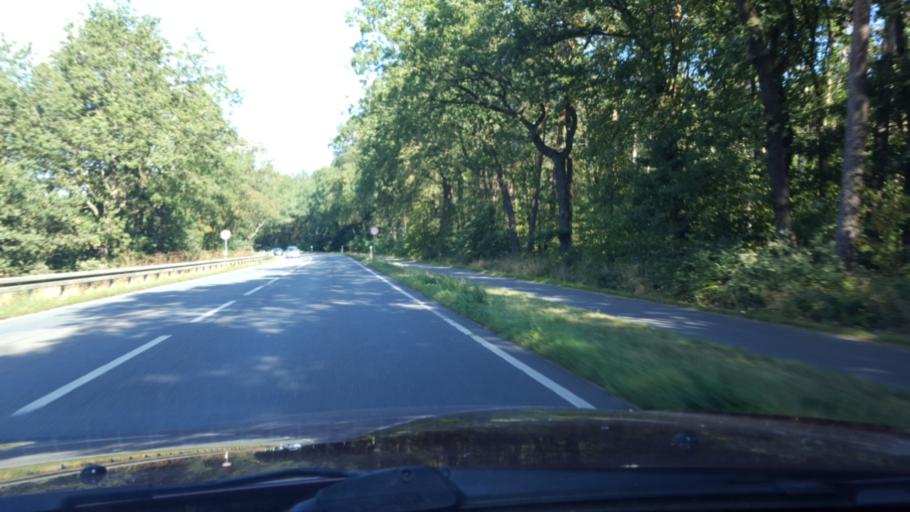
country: DE
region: Lower Saxony
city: Eystrup
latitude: 52.7937
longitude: 9.2122
